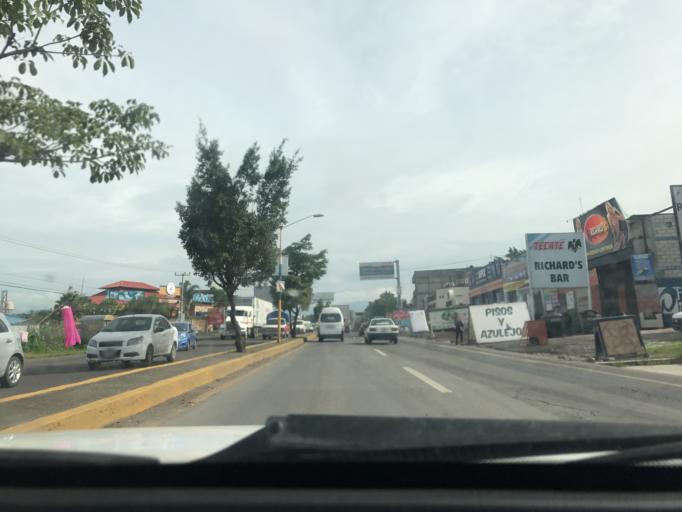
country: MX
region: Morelos
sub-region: Cuautla
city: Tierra Larga (Campo Nuevo)
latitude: 18.8559
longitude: -98.9357
